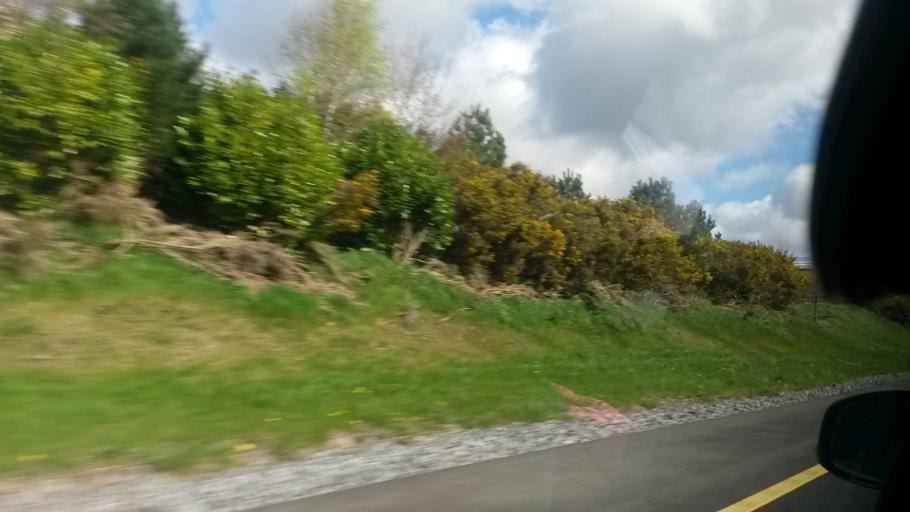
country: IE
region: Munster
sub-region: County Cork
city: Mitchelstown
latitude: 52.3085
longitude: -8.1547
